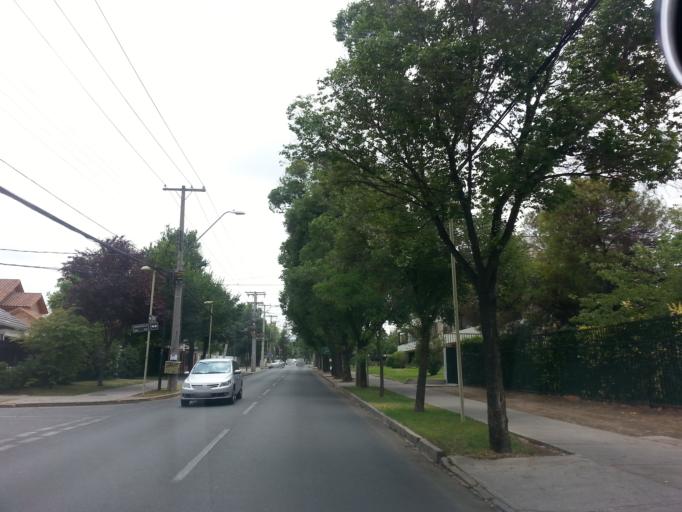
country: CL
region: Santiago Metropolitan
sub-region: Provincia de Santiago
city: Villa Presidente Frei, Nunoa, Santiago, Chile
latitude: -33.4149
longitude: -70.5593
